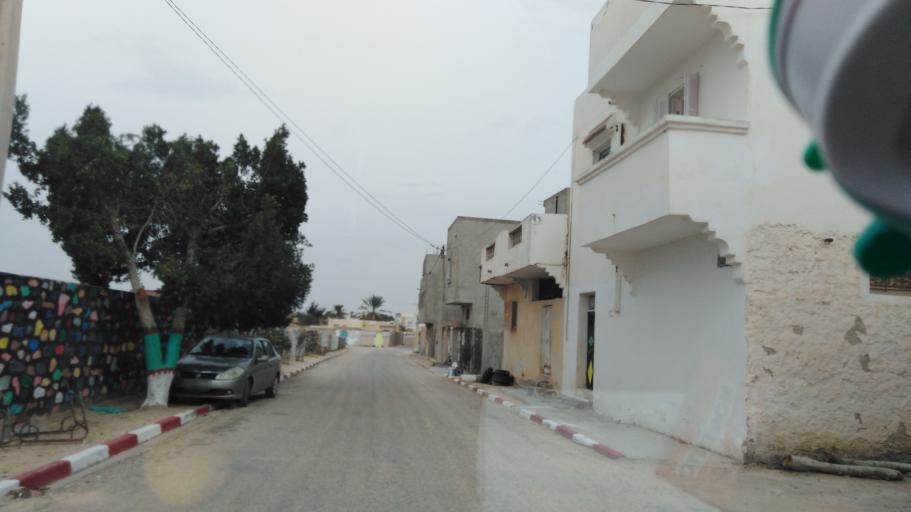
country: TN
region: Qabis
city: Gabes
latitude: 33.9560
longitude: 10.0027
